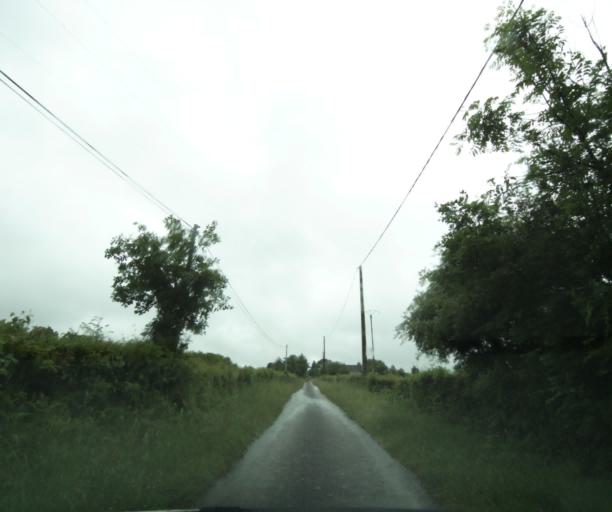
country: FR
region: Bourgogne
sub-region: Departement de Saone-et-Loire
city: Charolles
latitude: 46.4999
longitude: 4.3941
